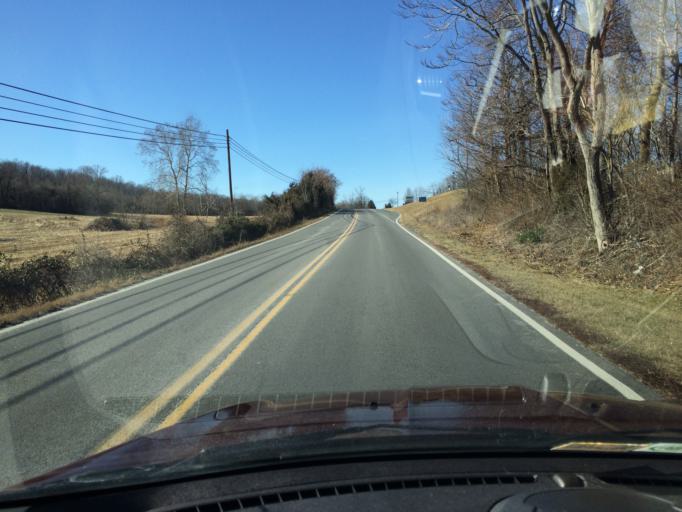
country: US
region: Virginia
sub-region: Rockingham County
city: Dayton
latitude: 38.4212
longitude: -78.9048
